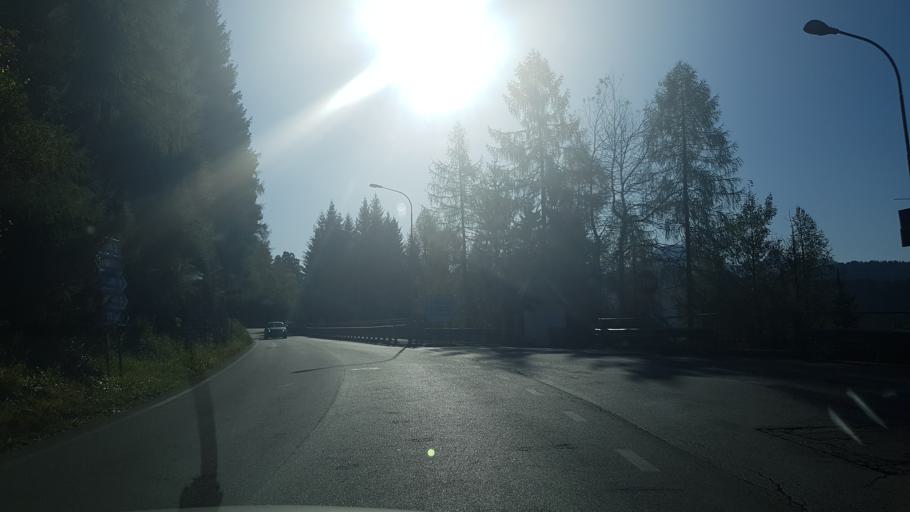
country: IT
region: Veneto
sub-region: Provincia di Belluno
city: Candide
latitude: 46.6042
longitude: 12.4843
